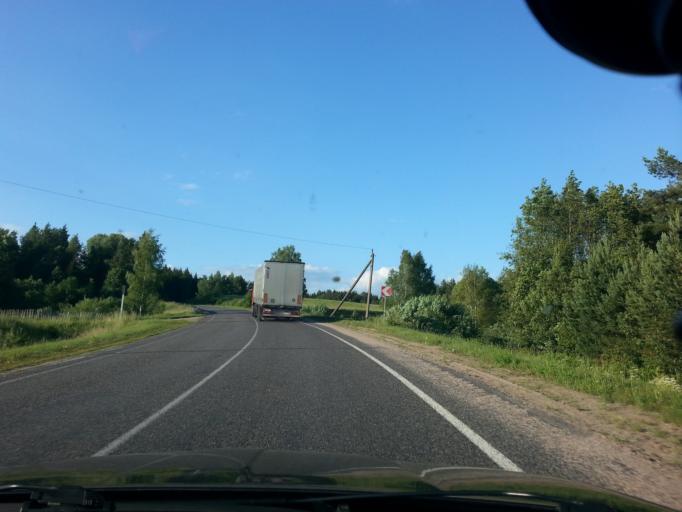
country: BY
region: Minsk
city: Svir
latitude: 54.8637
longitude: 26.3382
